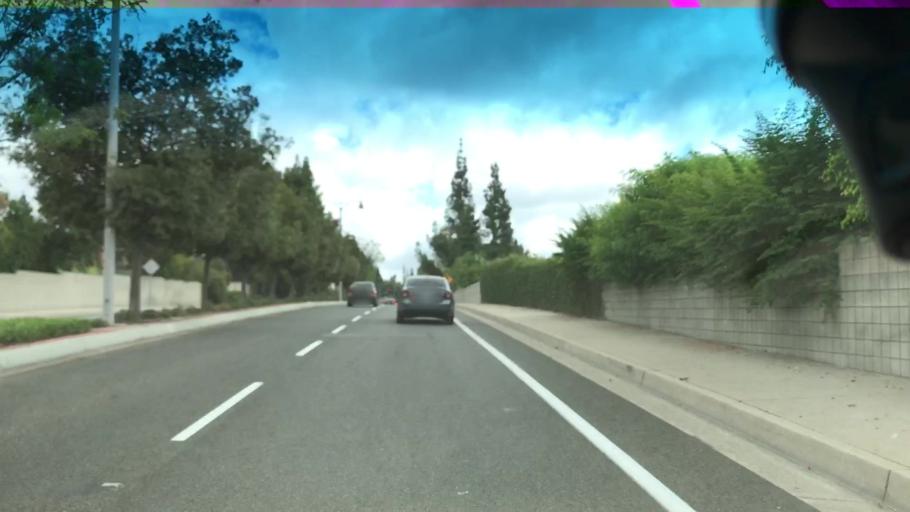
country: US
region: California
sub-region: Orange County
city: Mission Viejo
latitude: 33.6113
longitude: -117.6883
